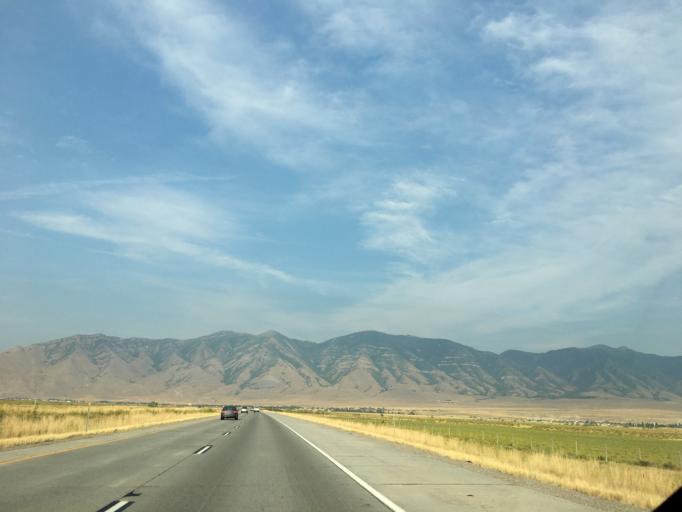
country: US
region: Utah
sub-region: Tooele County
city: Stansbury park
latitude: 40.6629
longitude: -112.3267
